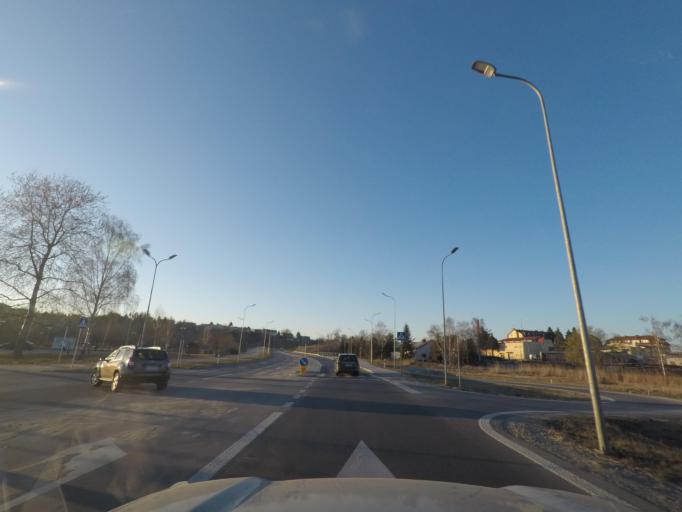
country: PL
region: Subcarpathian Voivodeship
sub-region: Powiat jasielski
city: Jaslo
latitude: 49.7364
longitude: 21.4847
